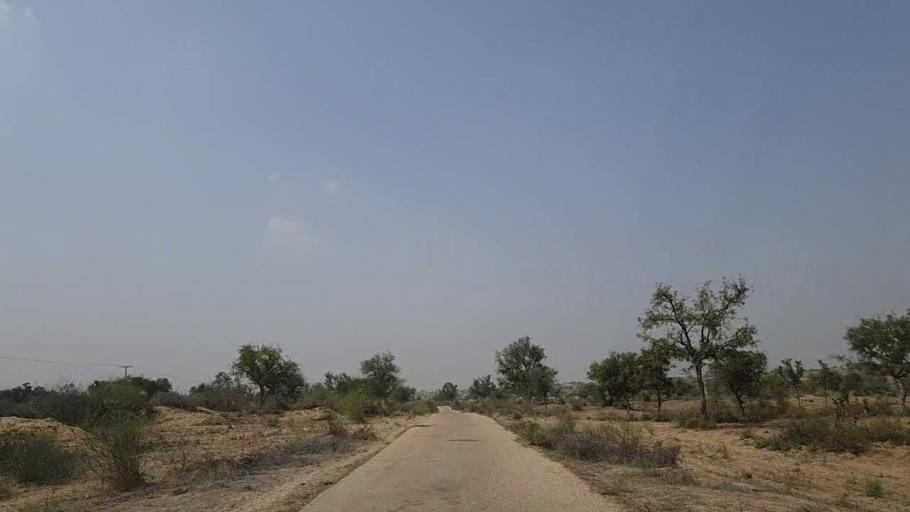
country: PK
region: Sindh
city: Mithi
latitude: 24.7646
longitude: 69.9136
